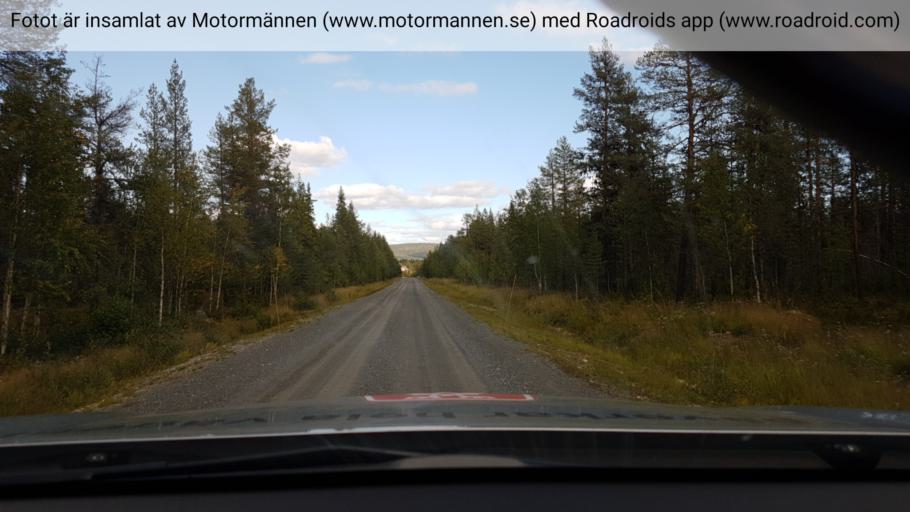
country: SE
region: Vaesterbotten
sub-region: Sorsele Kommun
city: Sorsele
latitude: 65.4598
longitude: 17.7452
